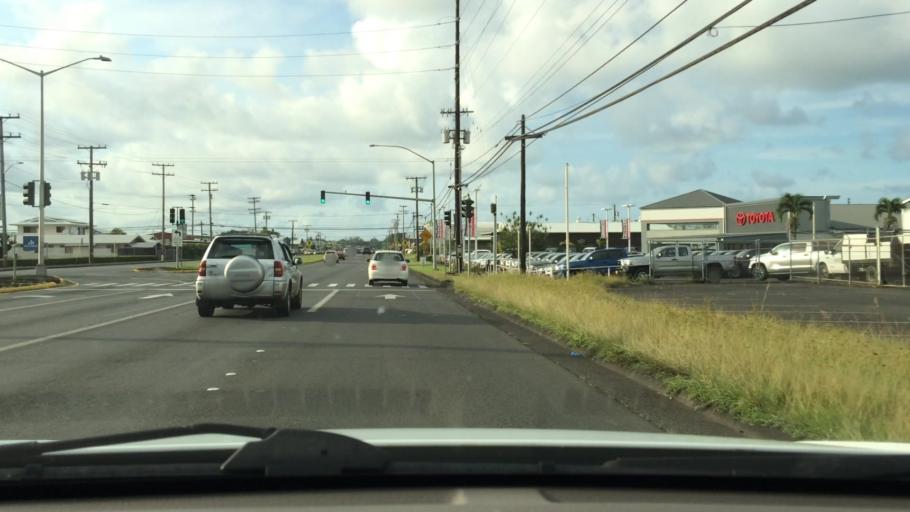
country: US
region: Hawaii
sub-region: Hawaii County
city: Hilo
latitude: 19.7054
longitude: -155.0641
